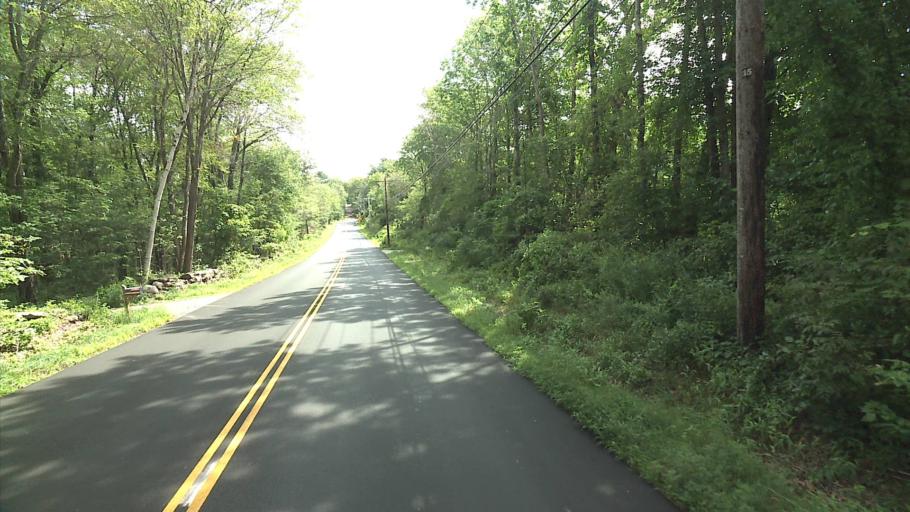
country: US
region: Connecticut
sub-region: Windham County
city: South Woodstock
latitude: 41.9486
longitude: -72.0145
